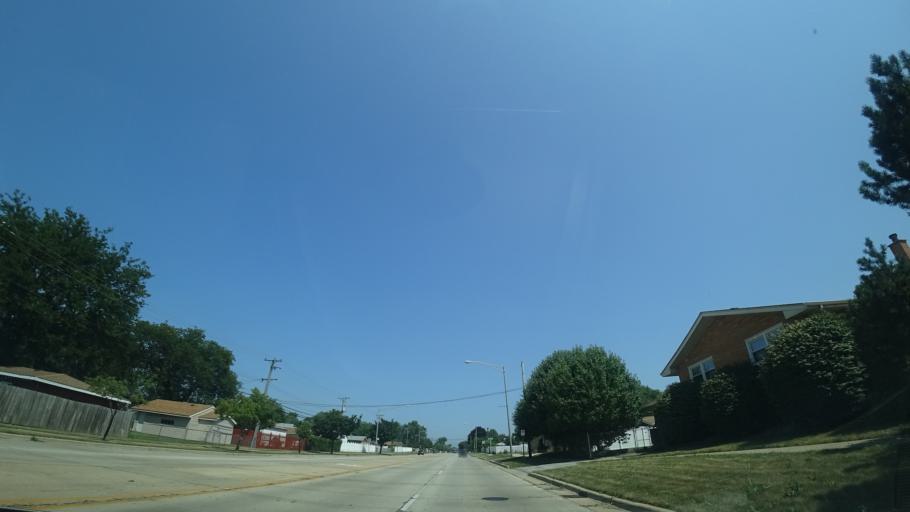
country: US
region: Illinois
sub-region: Cook County
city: Oak Lawn
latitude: 41.7052
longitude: -87.7585
